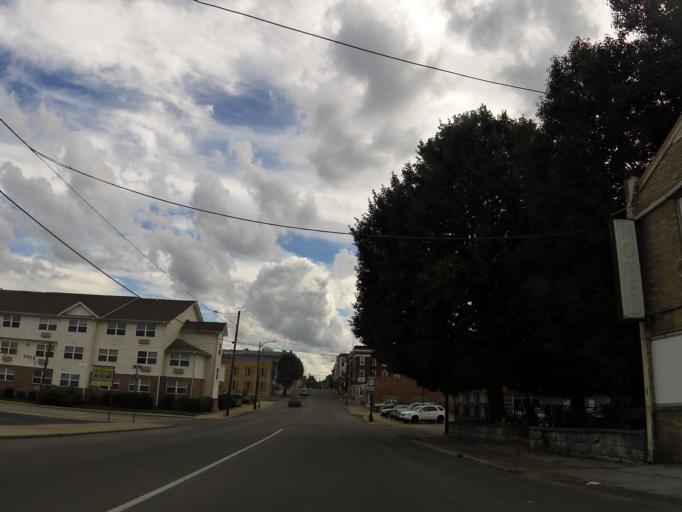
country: US
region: Kentucky
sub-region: Christian County
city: Hopkinsville
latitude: 36.8684
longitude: -87.4870
